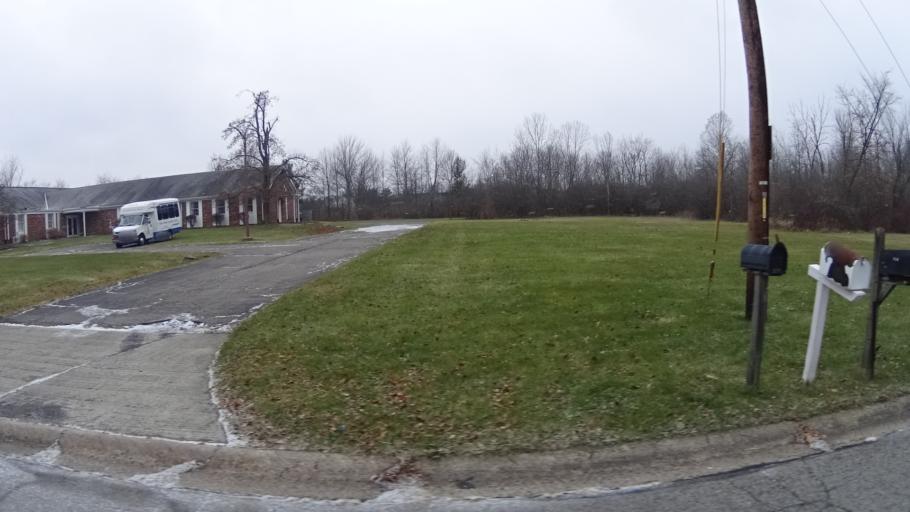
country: US
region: Ohio
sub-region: Lorain County
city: Oberlin
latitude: 41.2808
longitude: -82.2302
